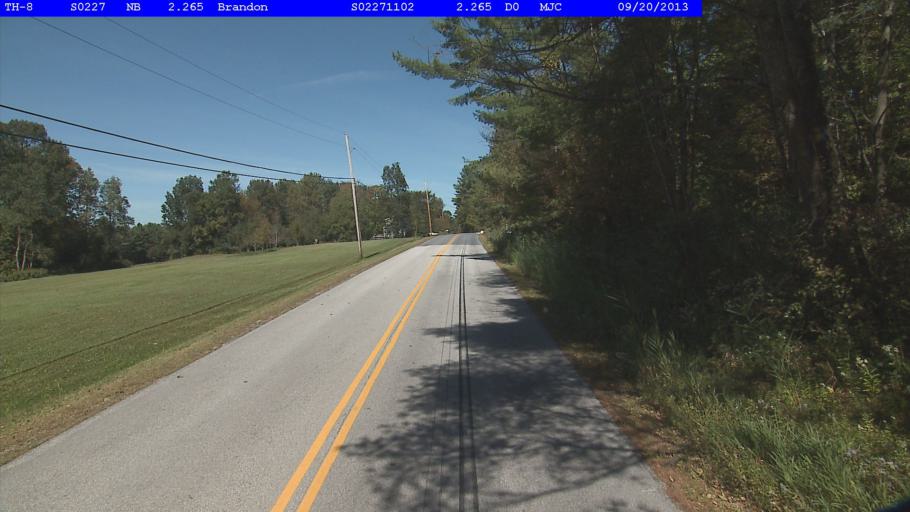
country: US
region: Vermont
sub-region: Rutland County
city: Brandon
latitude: 43.8070
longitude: -73.0564
